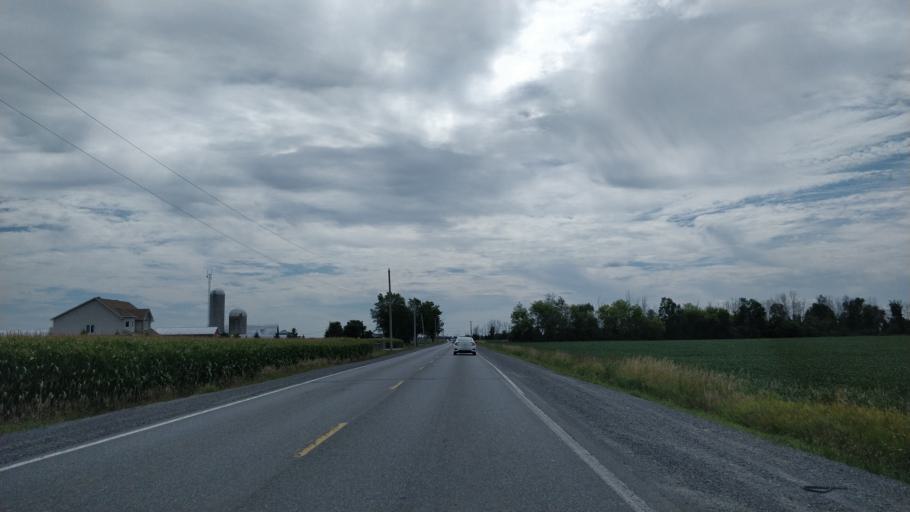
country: CA
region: Ontario
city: Bells Corners
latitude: 45.2574
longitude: -75.8514
